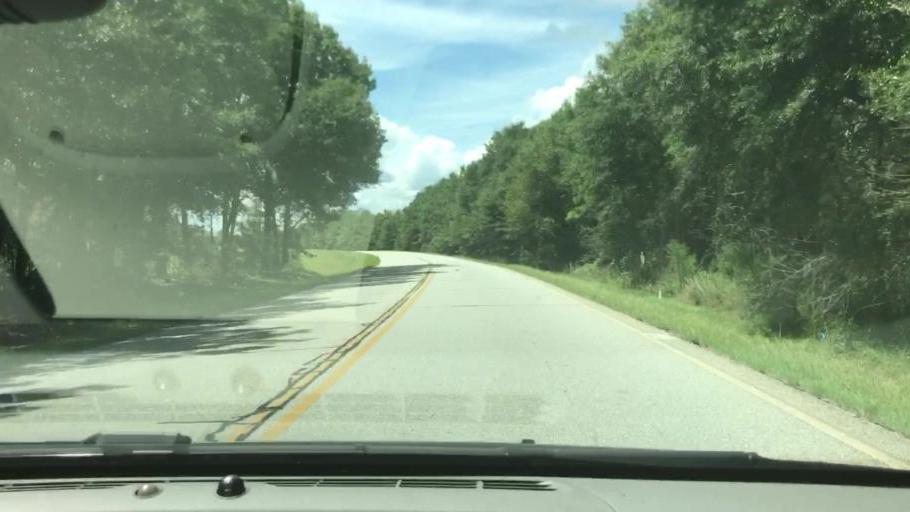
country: US
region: Georgia
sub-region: Stewart County
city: Lumpkin
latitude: 32.1385
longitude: -84.9696
